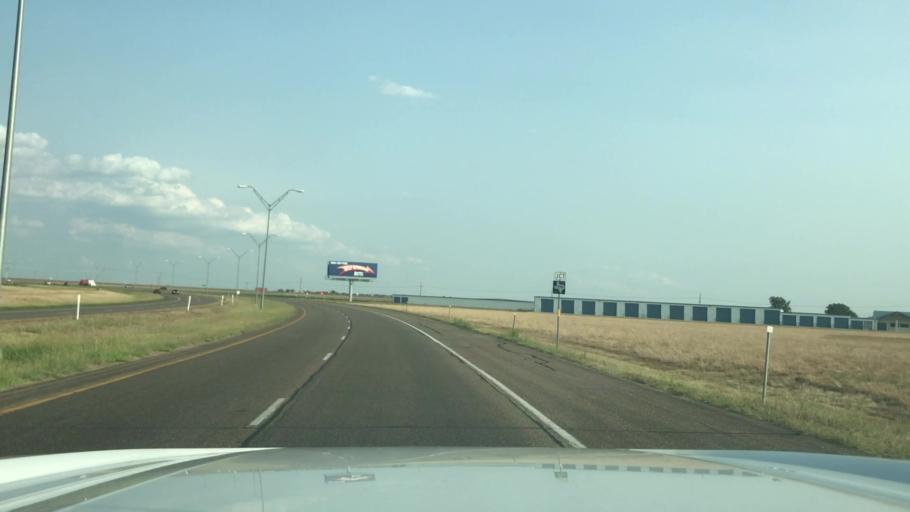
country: US
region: Texas
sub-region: Randall County
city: Canyon
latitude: 35.1208
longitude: -101.9373
